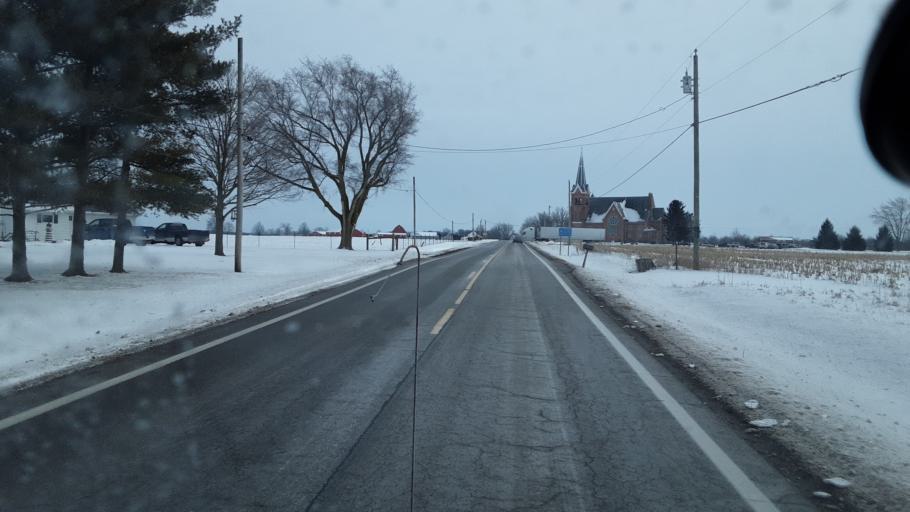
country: US
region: Ohio
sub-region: Union County
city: Marysville
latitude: 40.1914
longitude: -83.3533
